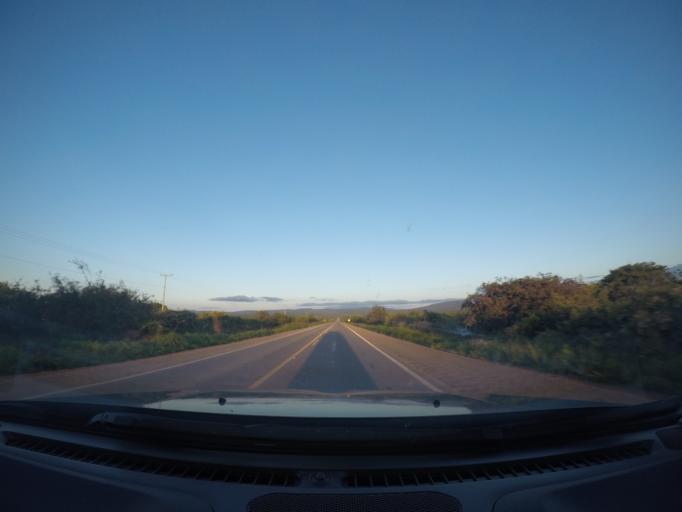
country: BR
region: Bahia
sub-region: Seabra
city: Seabra
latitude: -12.4035
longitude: -41.9515
